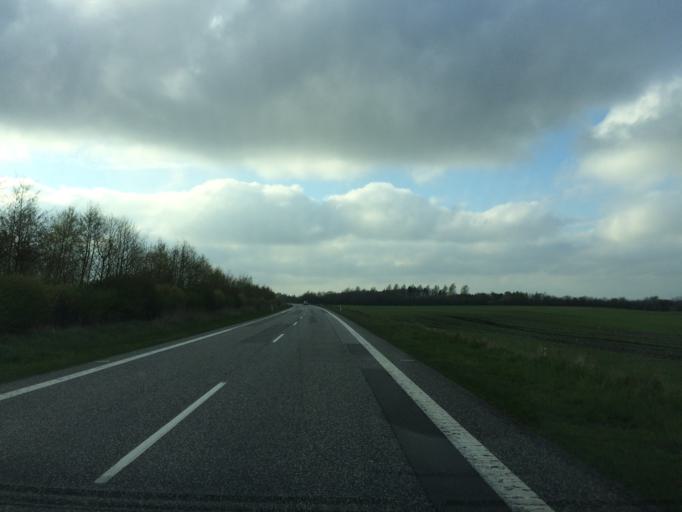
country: DK
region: Central Jutland
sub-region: Viborg Kommune
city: Karup
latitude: 56.3285
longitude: 9.1054
